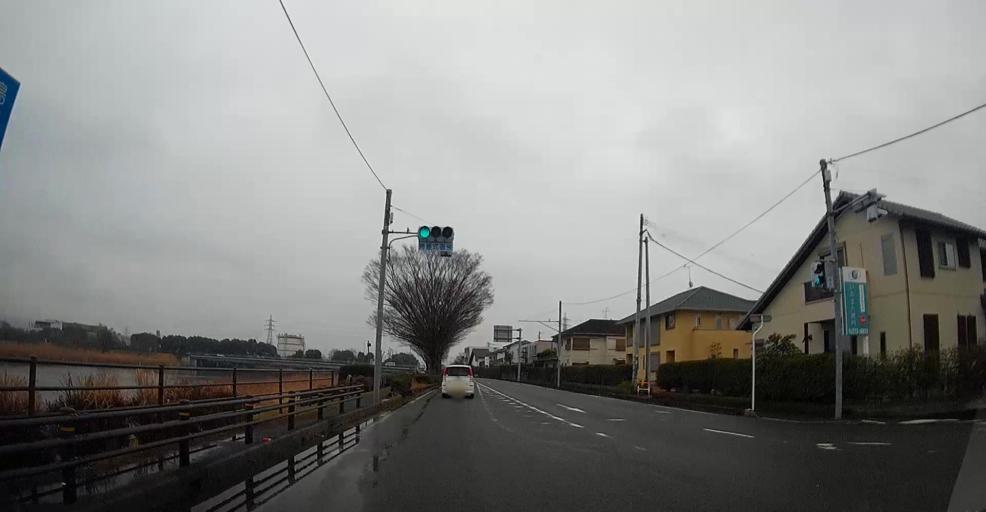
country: JP
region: Kumamoto
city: Kumamoto
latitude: 32.7664
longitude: 130.7516
